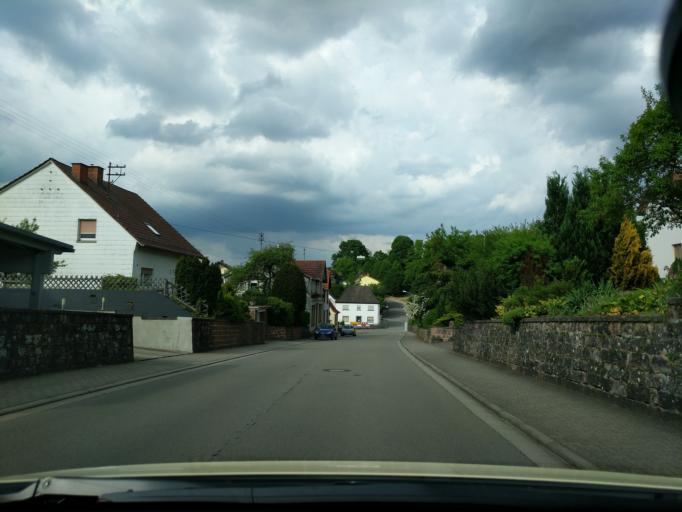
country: DE
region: Rheinland-Pfalz
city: Schopp
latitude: 49.3539
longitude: 7.6890
